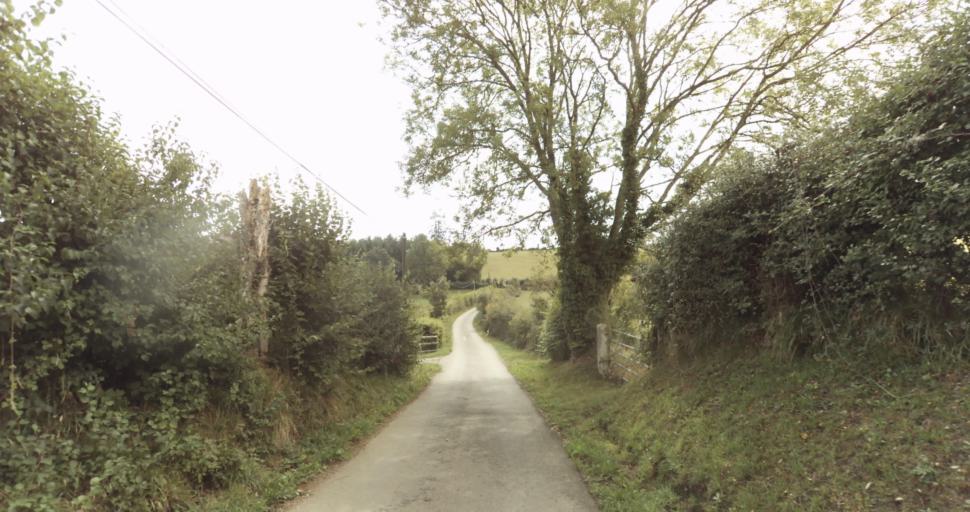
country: FR
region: Lower Normandy
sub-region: Departement de l'Orne
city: Gace
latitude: 48.8067
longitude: 0.2767
